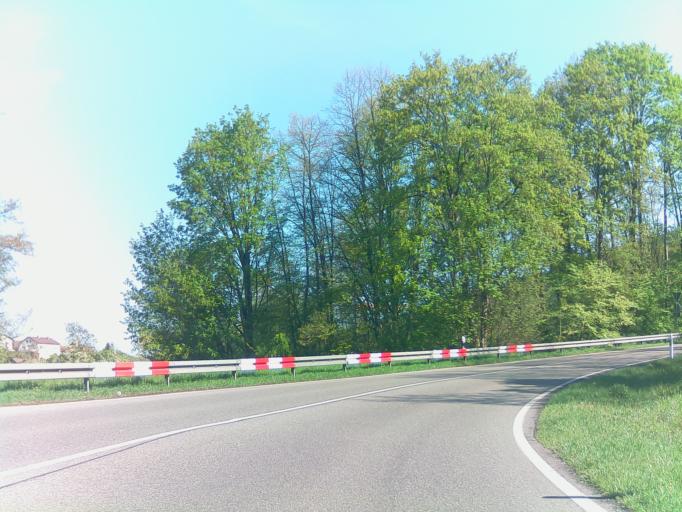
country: DE
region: Baden-Wuerttemberg
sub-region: Karlsruhe Region
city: Rohrdorf
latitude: 48.5619
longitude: 8.6976
